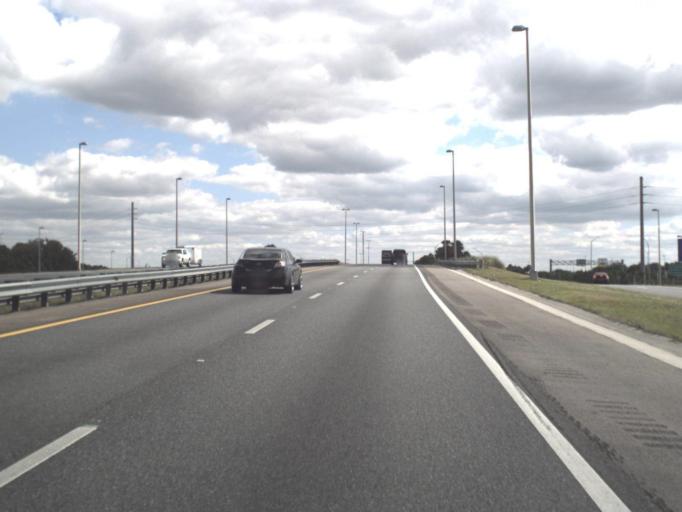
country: US
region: Florida
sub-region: Orange County
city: Oakland
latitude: 28.5501
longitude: -81.6422
